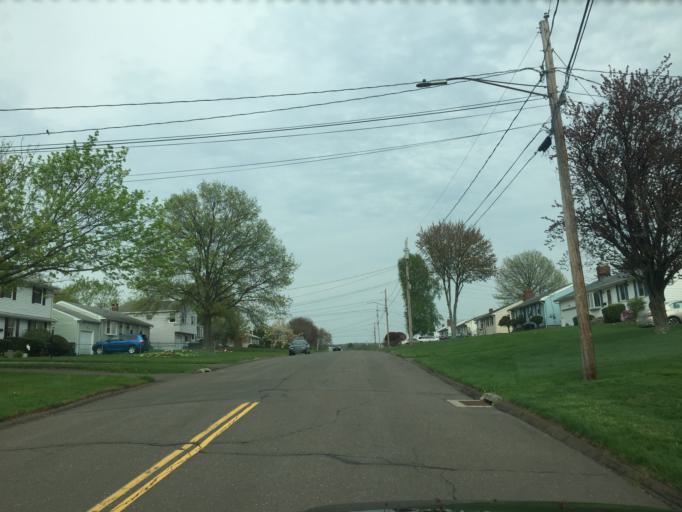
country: US
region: Connecticut
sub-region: Hartford County
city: Newington
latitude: 41.6962
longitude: -72.7436
